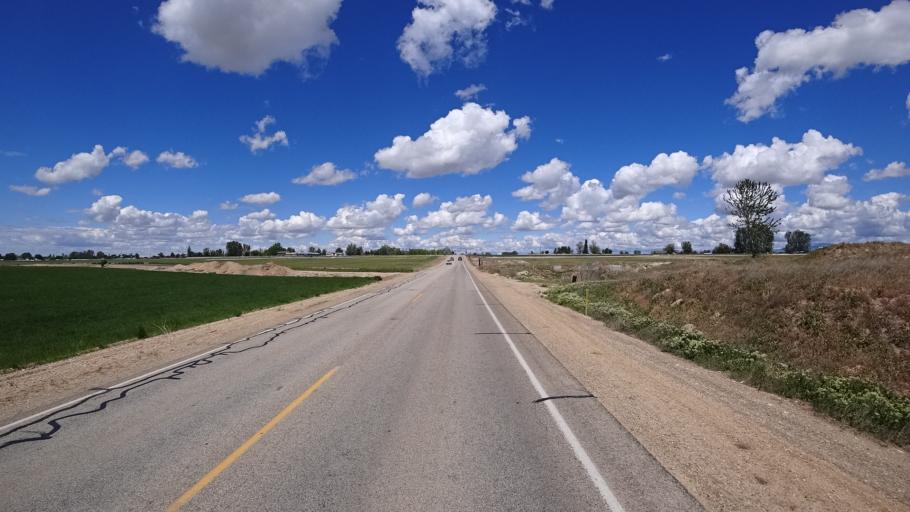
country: US
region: Idaho
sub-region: Ada County
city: Meridian
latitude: 43.5715
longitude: -116.4338
